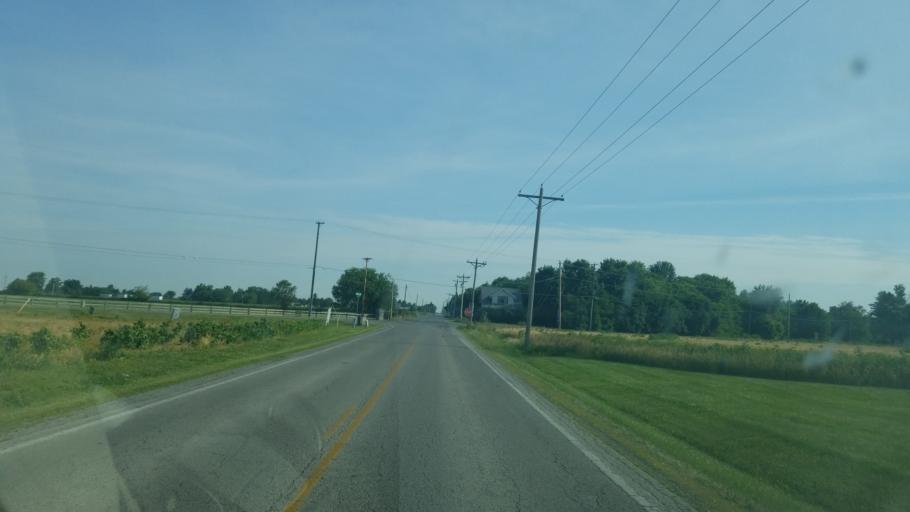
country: US
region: Ohio
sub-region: Hancock County
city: Findlay
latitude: 41.0027
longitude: -83.6985
